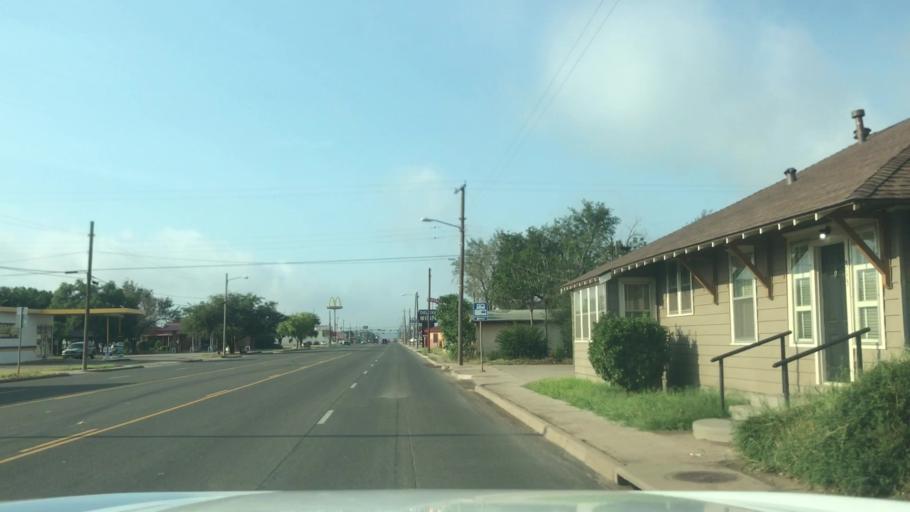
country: US
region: Texas
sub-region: Garza County
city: Post
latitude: 33.1947
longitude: -101.3784
